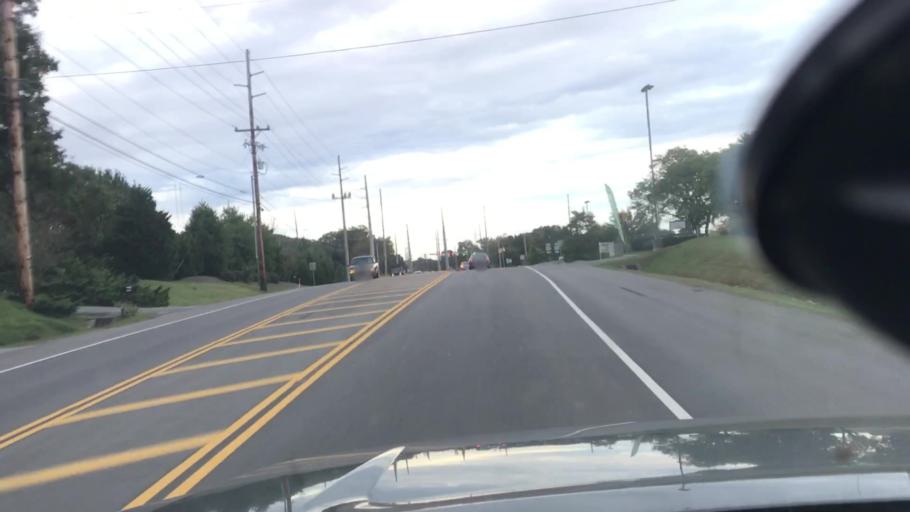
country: US
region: Tennessee
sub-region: Davidson County
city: Forest Hills
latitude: 36.0480
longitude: -86.8655
